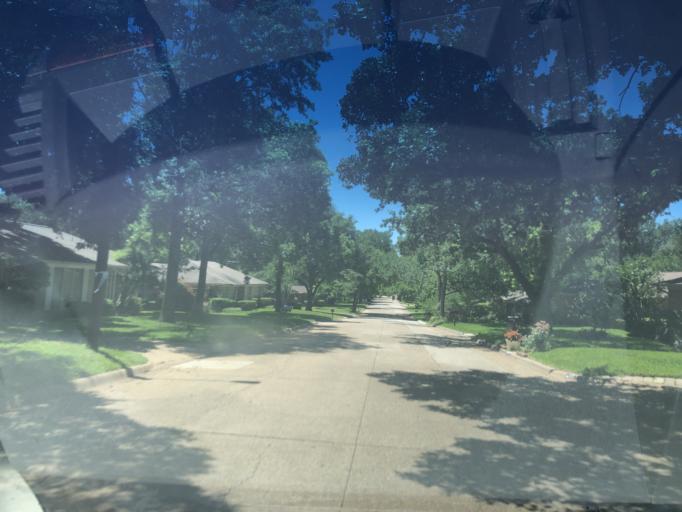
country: US
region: Texas
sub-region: Dallas County
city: Grand Prairie
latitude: 32.7773
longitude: -97.0357
